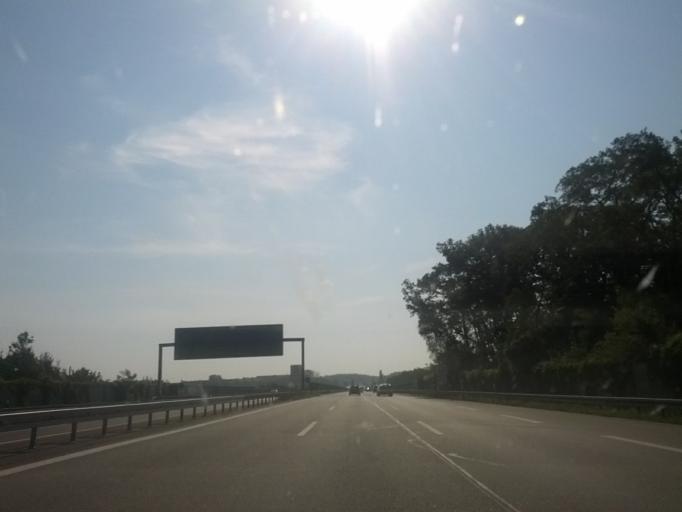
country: DE
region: Brandenburg
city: Woltersdorf
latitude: 52.4752
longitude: 13.7628
